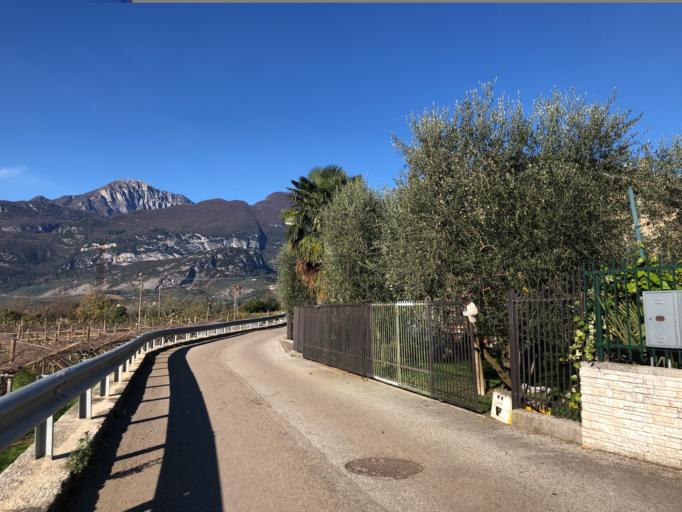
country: IT
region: Trentino-Alto Adige
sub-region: Provincia di Trento
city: Bolognano-Vignole
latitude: 45.9060
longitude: 10.8999
